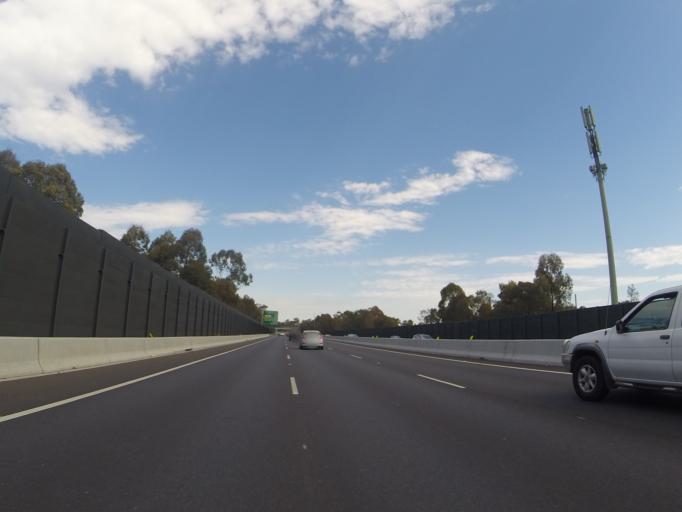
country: AU
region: New South Wales
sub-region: Campbelltown Municipality
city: Glenfield
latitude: -33.9423
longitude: 150.9008
